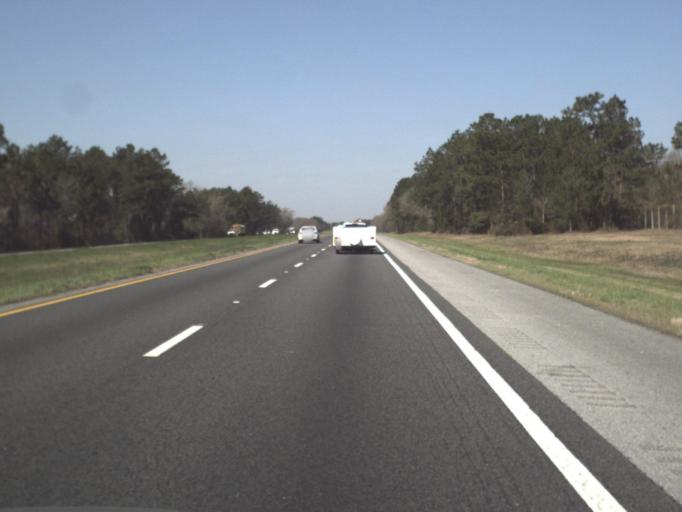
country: US
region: Florida
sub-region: Jackson County
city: Sneads
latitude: 30.6724
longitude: -85.0676
